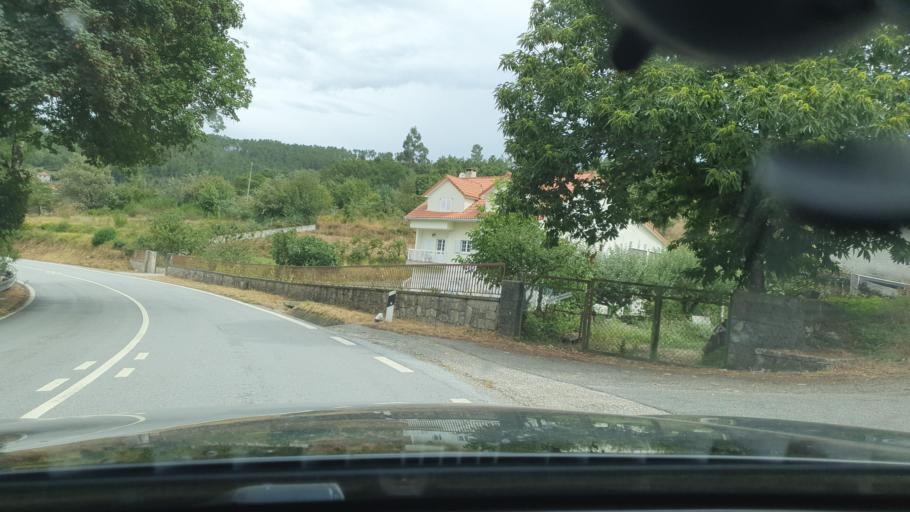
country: PT
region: Braga
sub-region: Cabeceiras de Basto
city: Cabeceiras de Basto
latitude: 41.6791
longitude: -7.9495
